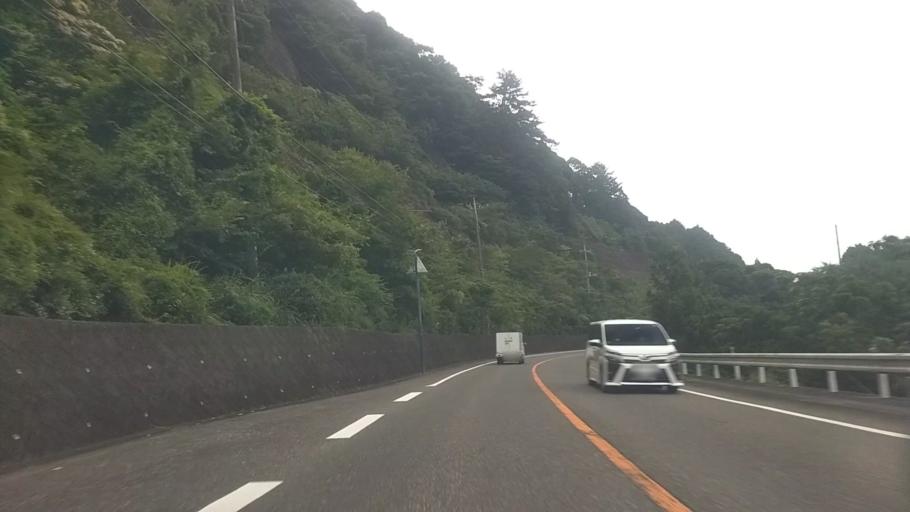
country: JP
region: Chiba
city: Kawaguchi
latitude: 35.1537
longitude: 140.0674
